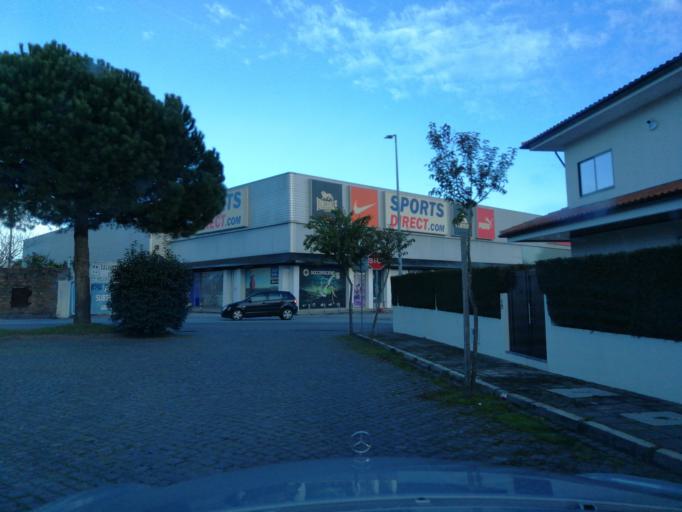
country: PT
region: Braga
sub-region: Braga
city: Braga
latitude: 41.5406
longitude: -8.4072
